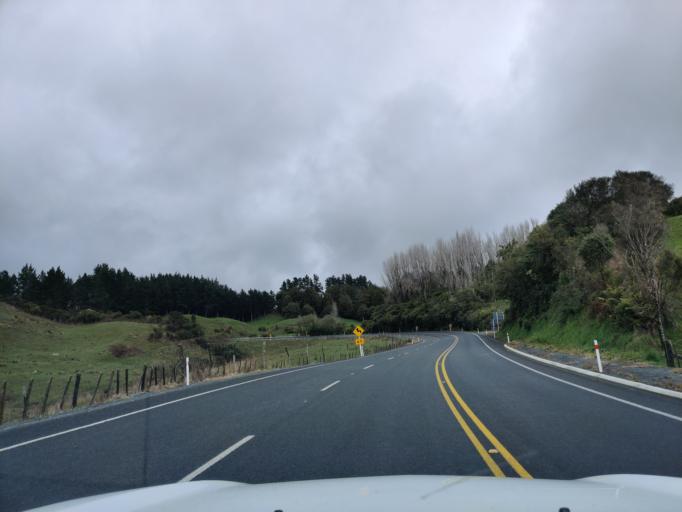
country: NZ
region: Waikato
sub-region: Otorohanga District
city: Otorohanga
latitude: -38.6352
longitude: 175.2071
